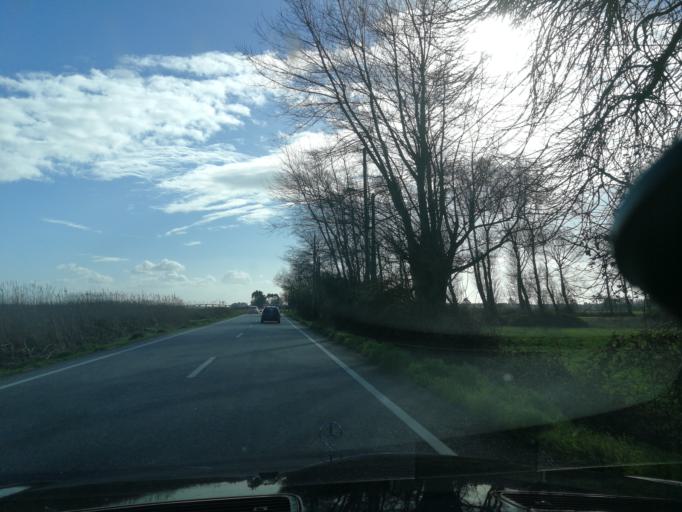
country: PT
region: Aveiro
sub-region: Estarreja
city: Pardilho
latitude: 40.8110
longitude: -8.6714
